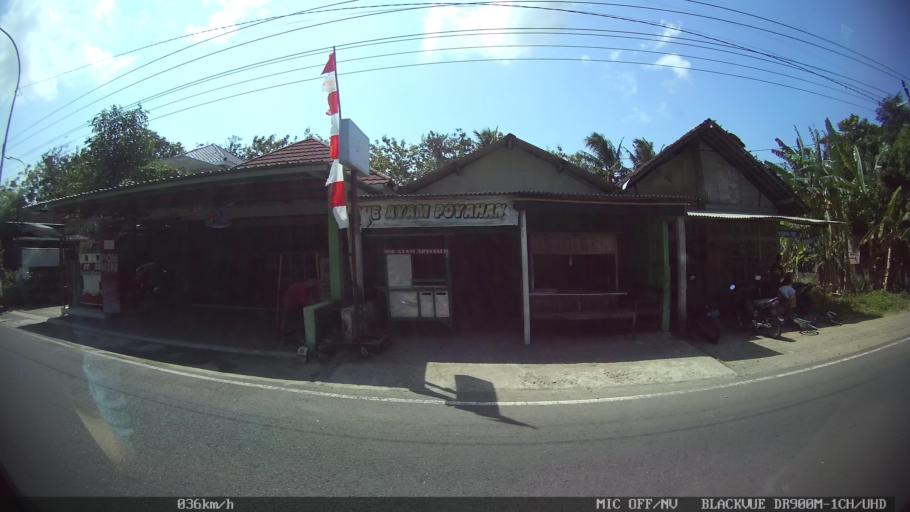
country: ID
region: Daerah Istimewa Yogyakarta
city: Pundong
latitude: -7.9869
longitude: 110.3275
